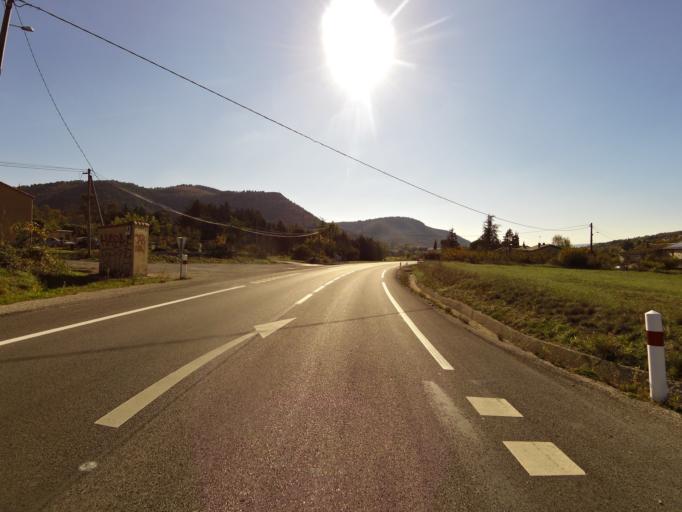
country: FR
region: Rhone-Alpes
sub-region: Departement de l'Ardeche
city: Vesseaux
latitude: 44.6589
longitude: 4.4493
